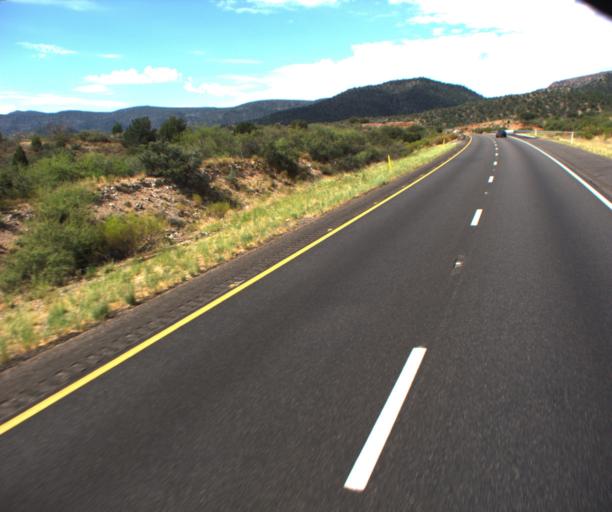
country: US
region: Arizona
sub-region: Yavapai County
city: Camp Verde
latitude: 34.5617
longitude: -111.9048
